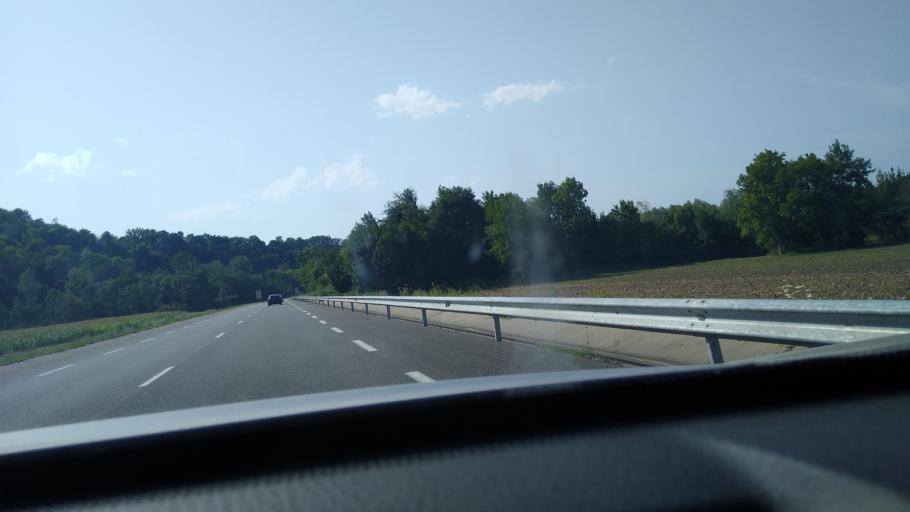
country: FR
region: Midi-Pyrenees
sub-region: Departement de la Haute-Garonne
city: Salies-du-Salat
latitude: 43.0347
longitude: 1.0014
